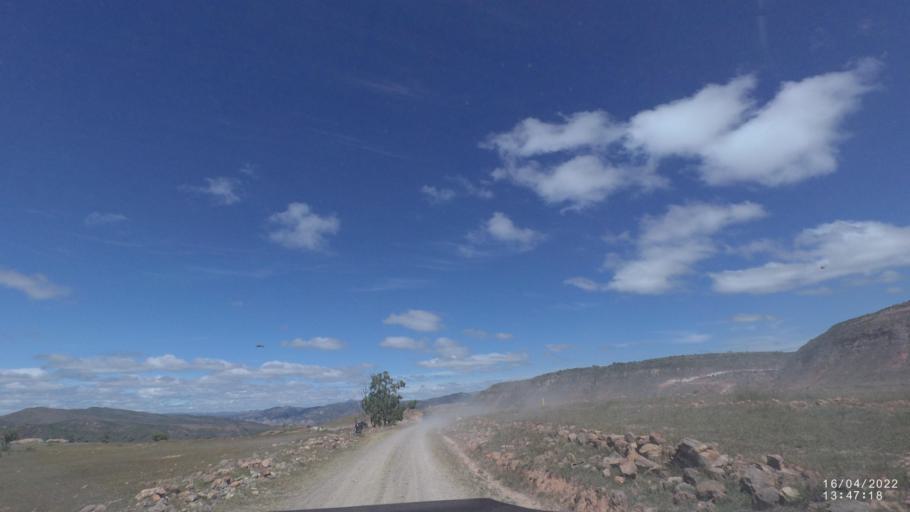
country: BO
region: Cochabamba
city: Mizque
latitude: -18.0076
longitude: -65.5838
